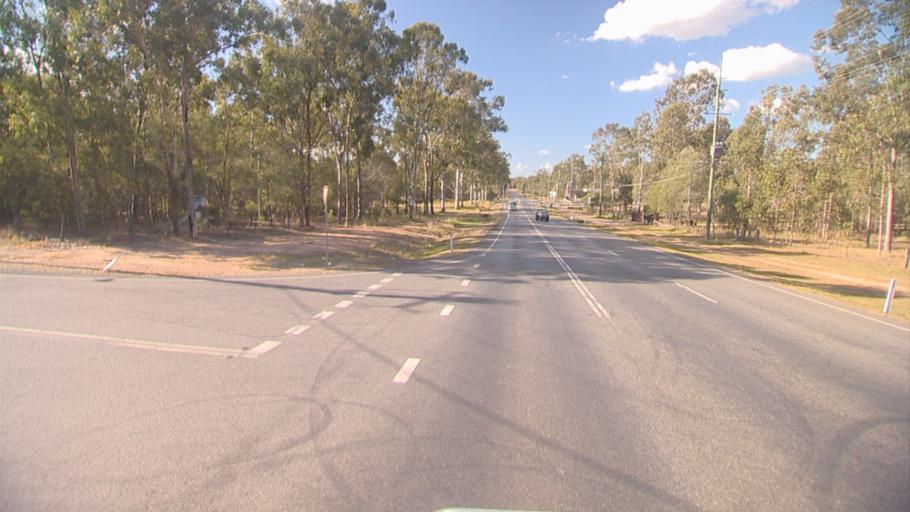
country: AU
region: Queensland
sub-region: Logan
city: North Maclean
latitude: -27.8136
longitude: 152.9755
